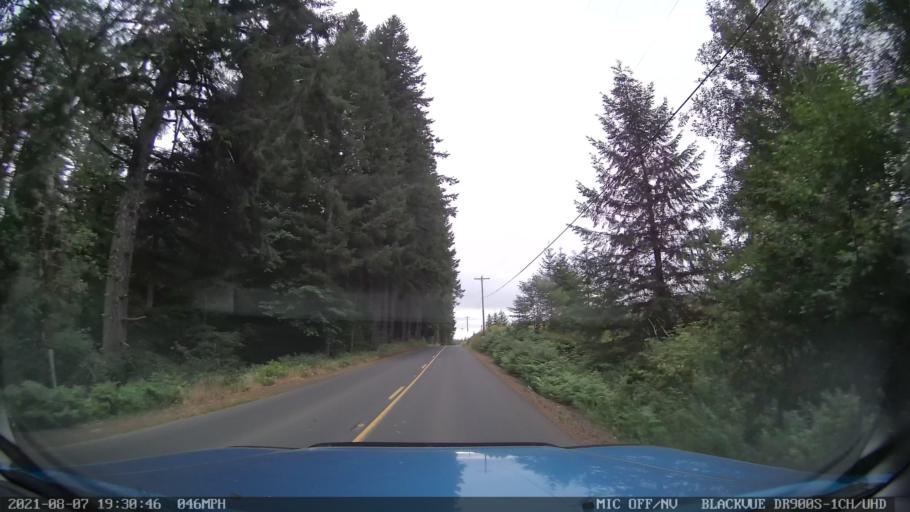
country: US
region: Oregon
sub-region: Linn County
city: Lyons
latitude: 44.8872
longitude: -122.6250
